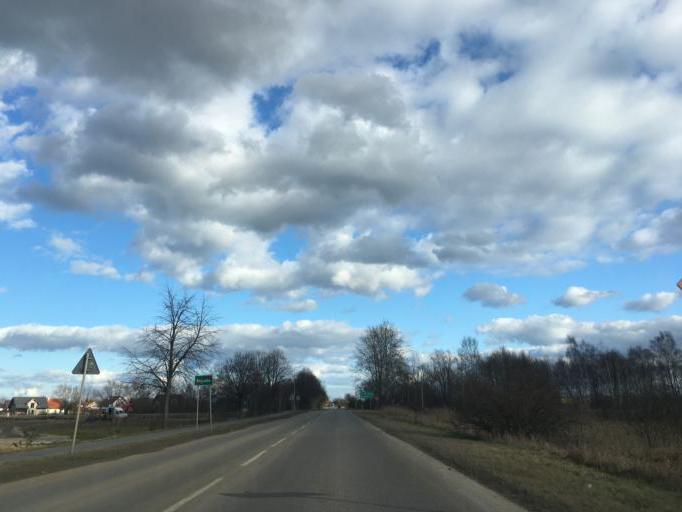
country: PL
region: Pomeranian Voivodeship
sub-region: Powiat gdanski
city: Cedry Wielkie
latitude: 54.3298
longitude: 18.7863
